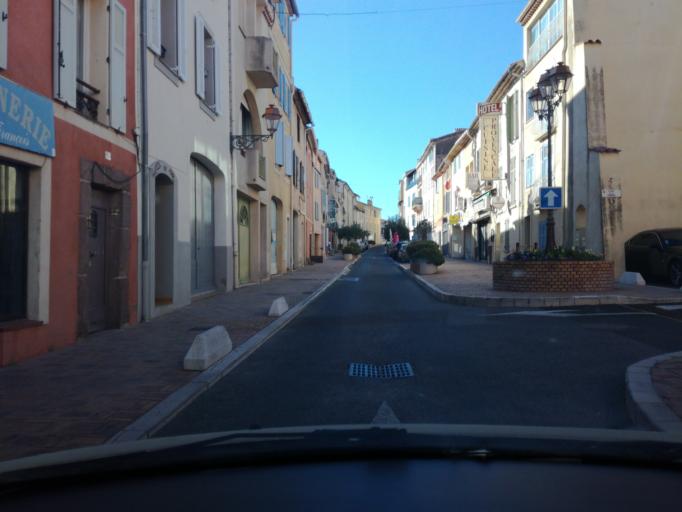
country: FR
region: Provence-Alpes-Cote d'Azur
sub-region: Departement du Var
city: Puget-sur-Argens
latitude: 43.4547
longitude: 6.6866
